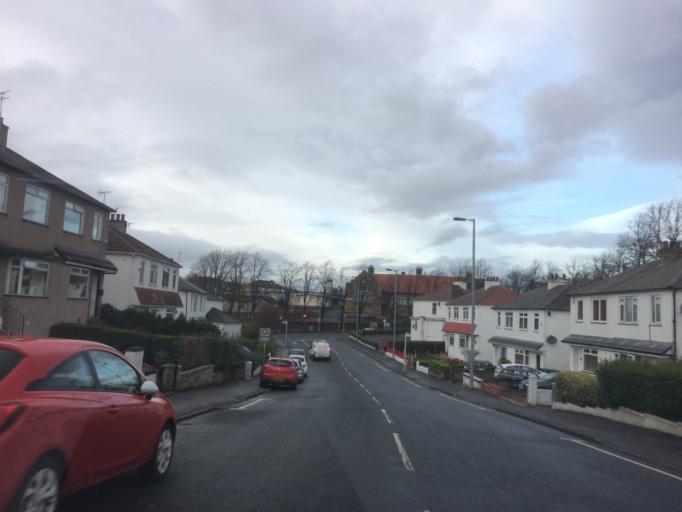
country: GB
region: Scotland
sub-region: East Renfrewshire
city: Giffnock
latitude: 55.8084
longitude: -4.3122
